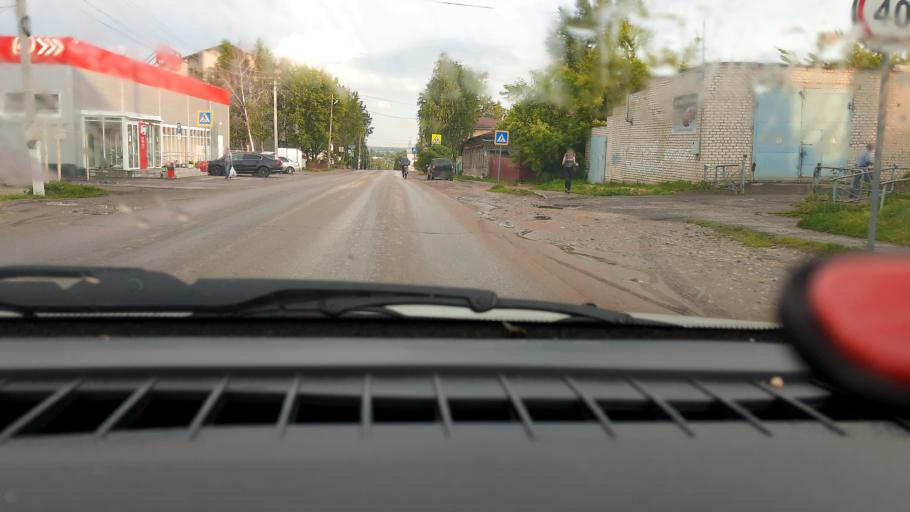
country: RU
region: Nizjnij Novgorod
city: Lukoyanov
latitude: 55.0370
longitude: 44.4944
